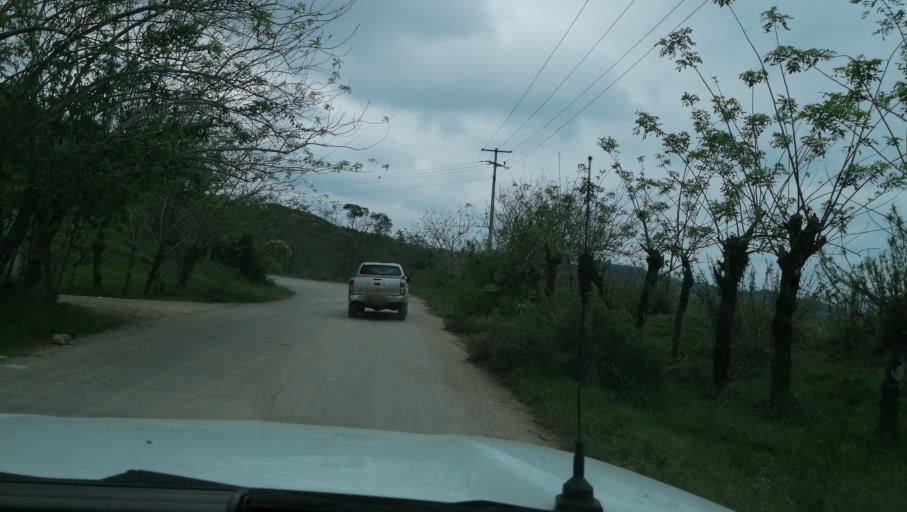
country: MX
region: Chiapas
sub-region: Francisco Leon
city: San Miguel la Sardina
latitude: 17.2699
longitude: -93.2637
